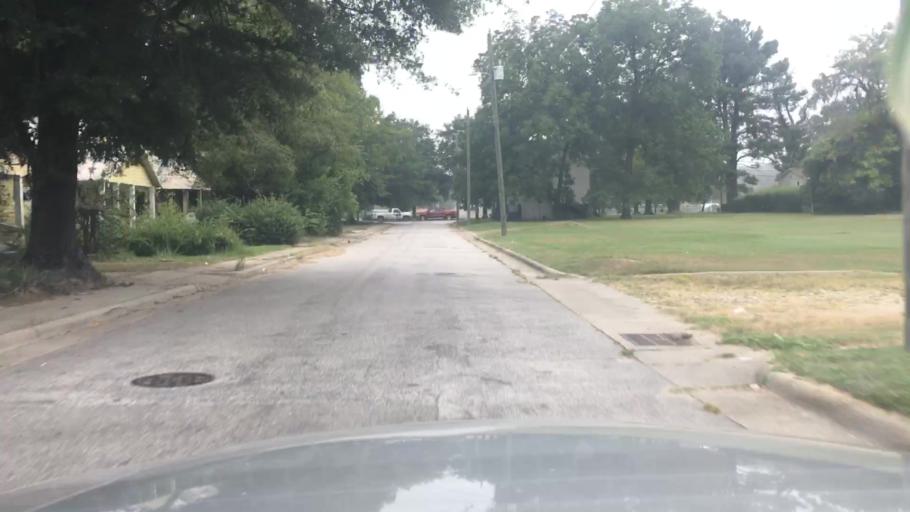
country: US
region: North Carolina
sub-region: Cumberland County
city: Fayetteville
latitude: 35.0577
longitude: -78.8753
